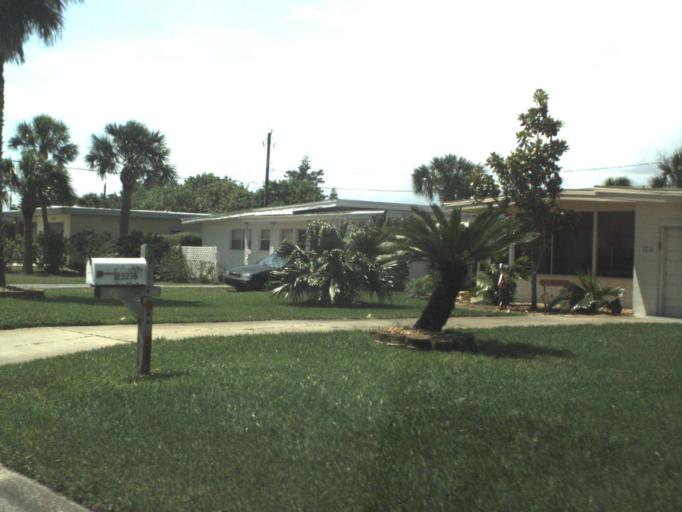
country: US
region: Florida
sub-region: Volusia County
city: Daytona Beach Shores
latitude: 29.1570
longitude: -80.9755
